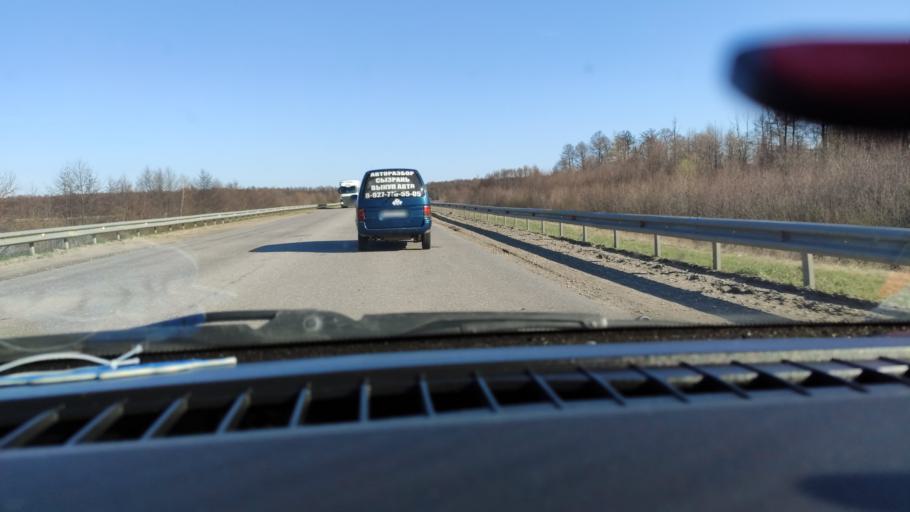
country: RU
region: Samara
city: Varlamovo
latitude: 53.1386
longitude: 48.2856
